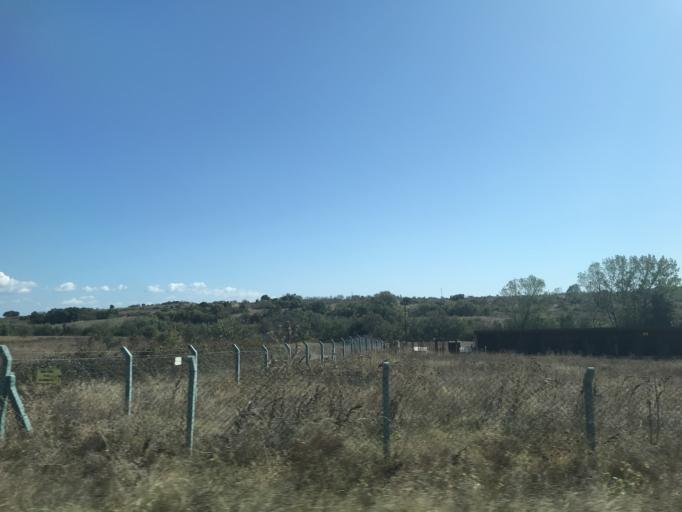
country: TR
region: Kirklareli
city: Kirklareli
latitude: 41.7832
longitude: 27.2313
